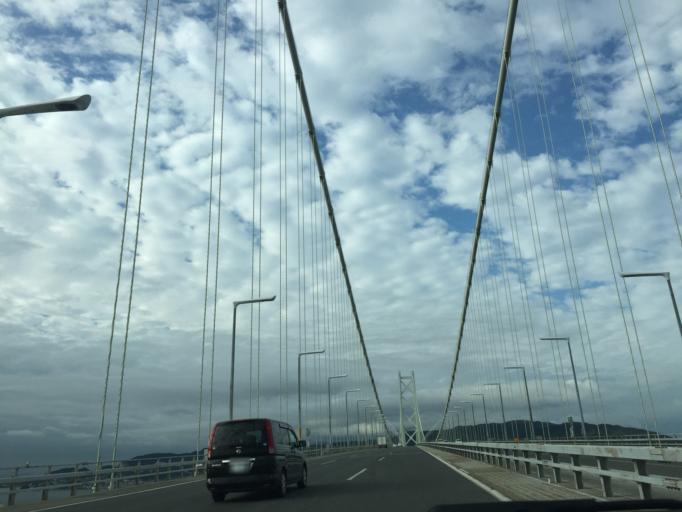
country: JP
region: Hyogo
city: Akashi
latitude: 34.6213
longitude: 135.0251
